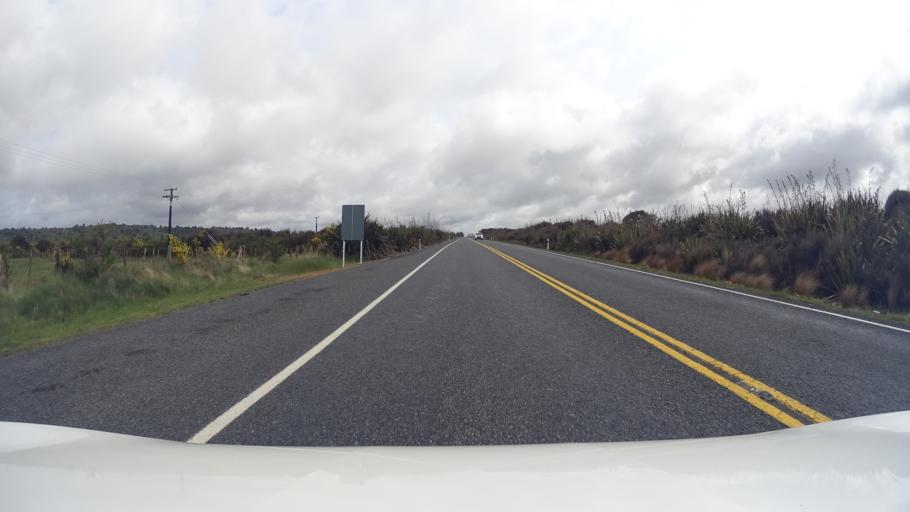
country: NZ
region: Manawatu-Wanganui
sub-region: Ruapehu District
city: Waiouru
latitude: -39.1960
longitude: 175.4013
